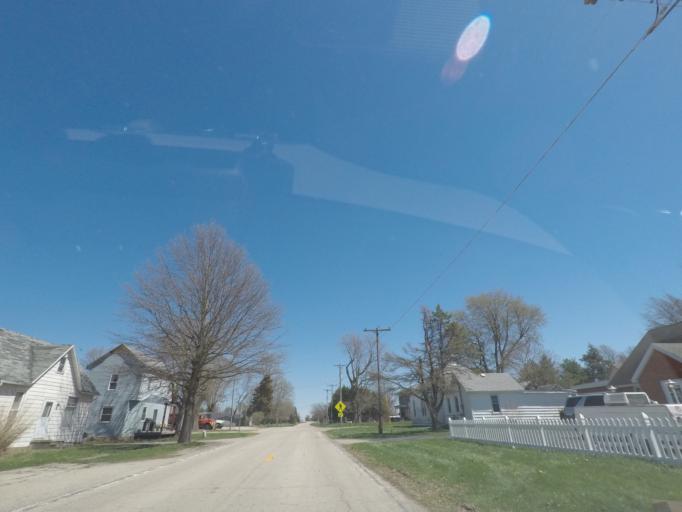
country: US
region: Illinois
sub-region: Macon County
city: Warrensburg
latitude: 39.9685
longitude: -89.1609
